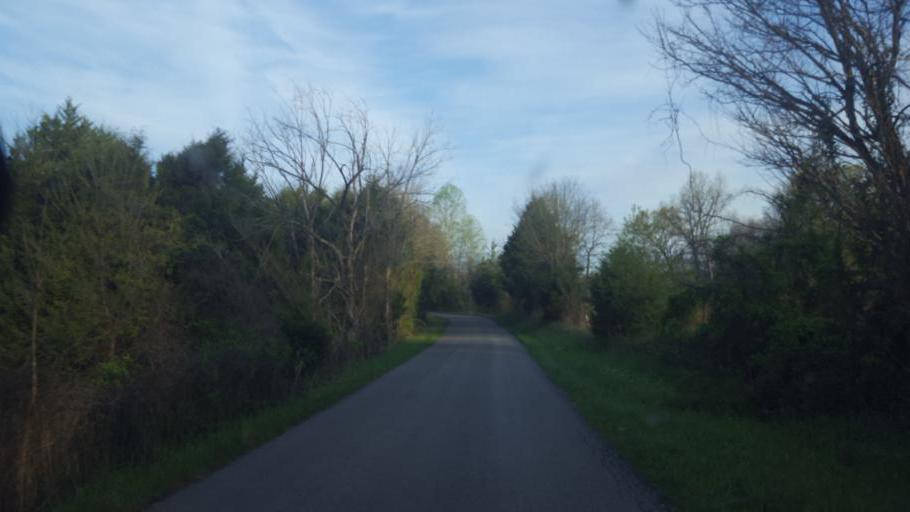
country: US
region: Kentucky
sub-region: Barren County
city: Cave City
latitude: 37.2020
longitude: -86.0189
